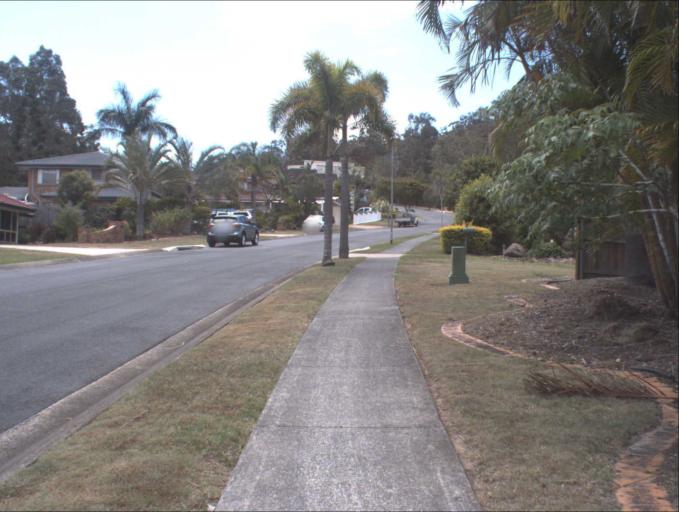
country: AU
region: Queensland
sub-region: Logan
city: Slacks Creek
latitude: -27.6414
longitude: 153.1810
